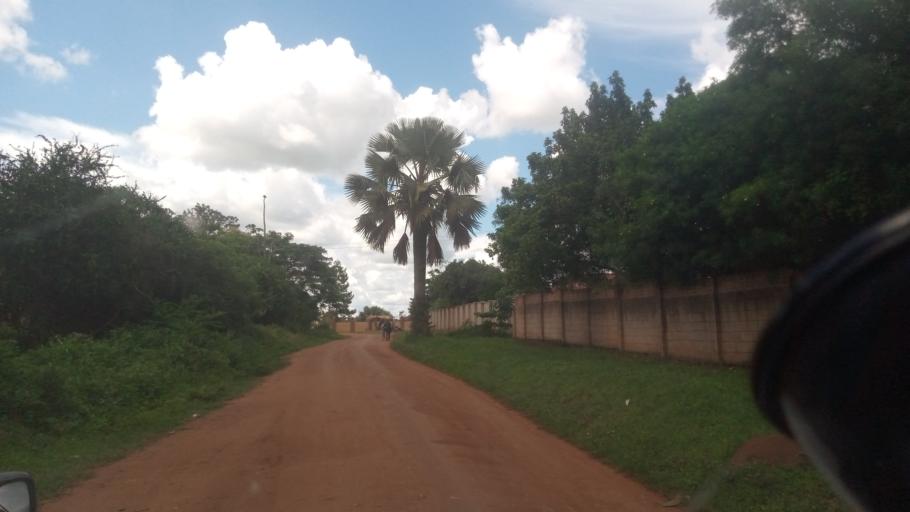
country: UG
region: Northern Region
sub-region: Lira District
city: Lira
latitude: 2.2392
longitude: 32.9032
